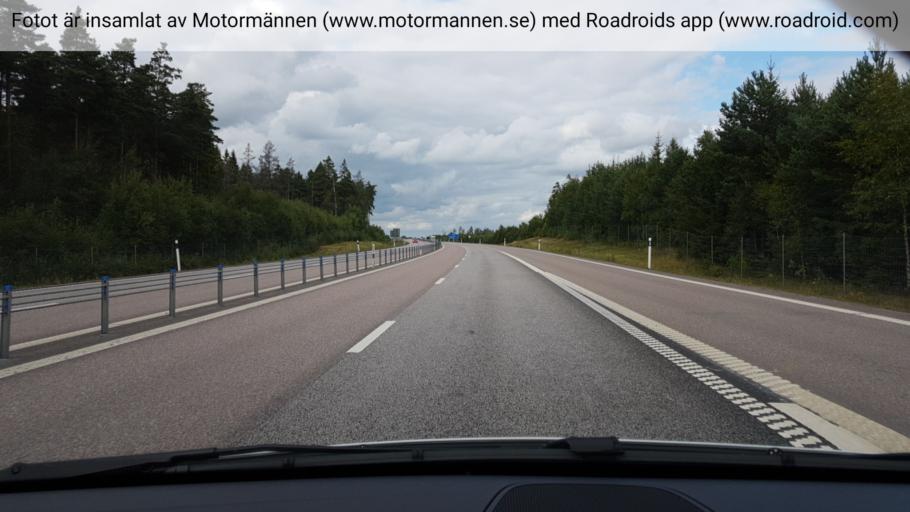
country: SE
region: Vaestra Goetaland
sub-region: Skovde Kommun
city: Skultorp
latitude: 58.3419
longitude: 13.8649
